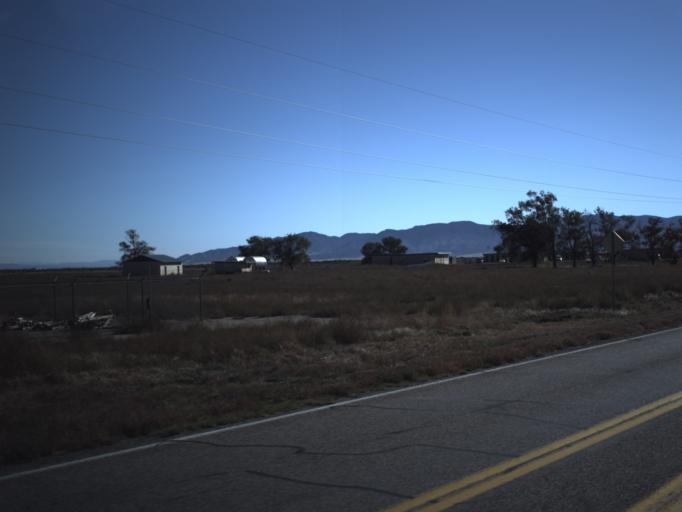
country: US
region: Utah
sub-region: Washington County
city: Enterprise
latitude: 37.7085
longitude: -113.6536
